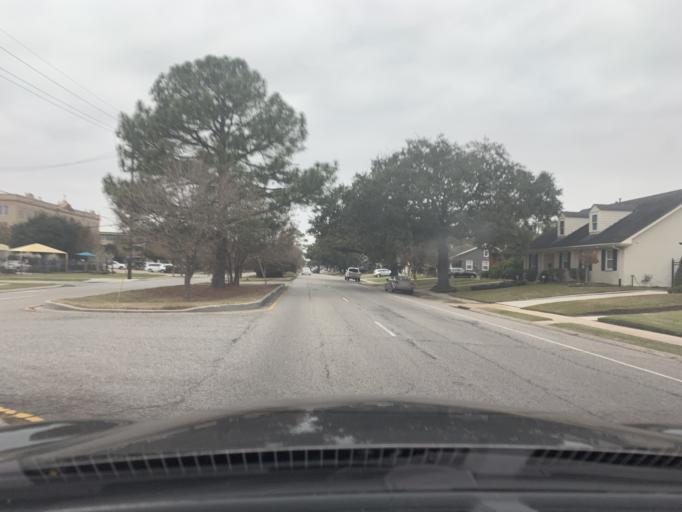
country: US
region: Louisiana
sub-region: Jefferson Parish
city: Metairie
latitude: 30.0197
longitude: -90.1081
